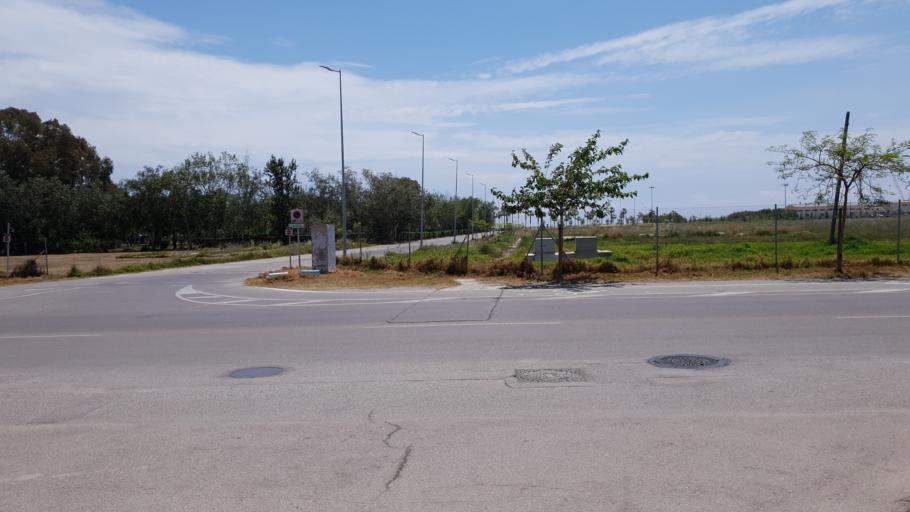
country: ES
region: Valencia
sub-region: Provincia de Castello
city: Burriana
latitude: 39.8675
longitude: -0.0696
